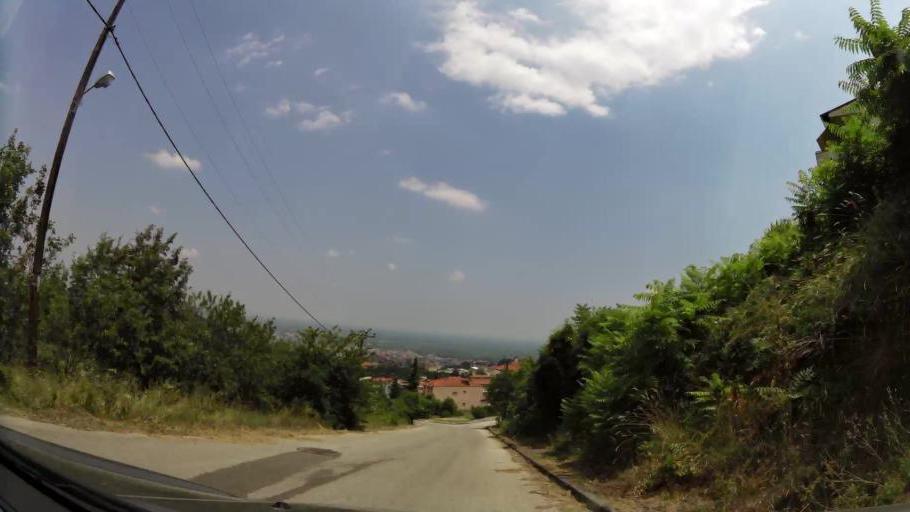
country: GR
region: Central Macedonia
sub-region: Nomos Imathias
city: Veroia
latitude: 40.5147
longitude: 22.1826
